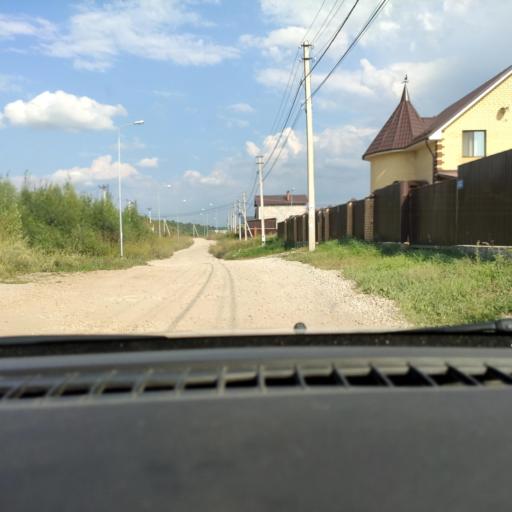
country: RU
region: Perm
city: Perm
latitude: 58.0285
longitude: 56.3448
